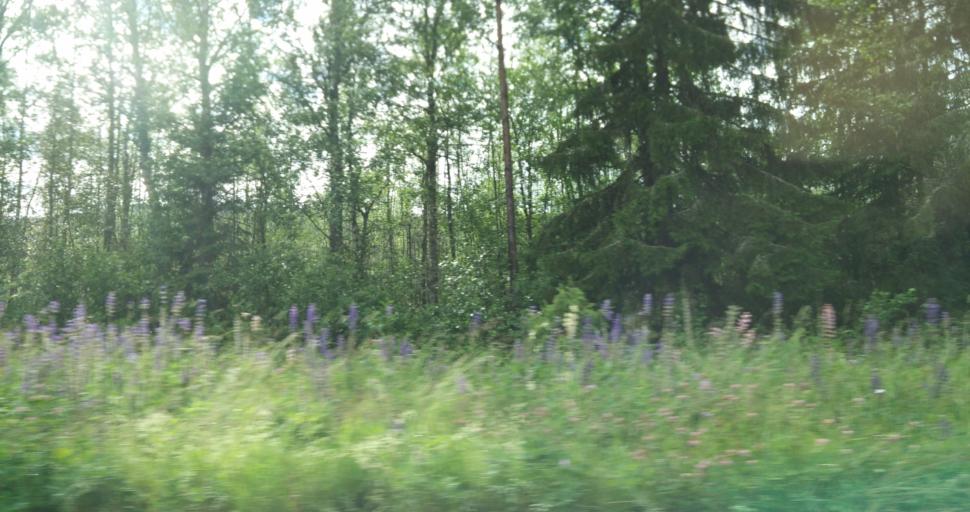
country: SE
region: Vaermland
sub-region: Hagfors Kommun
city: Ekshaerad
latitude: 60.0362
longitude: 13.4926
